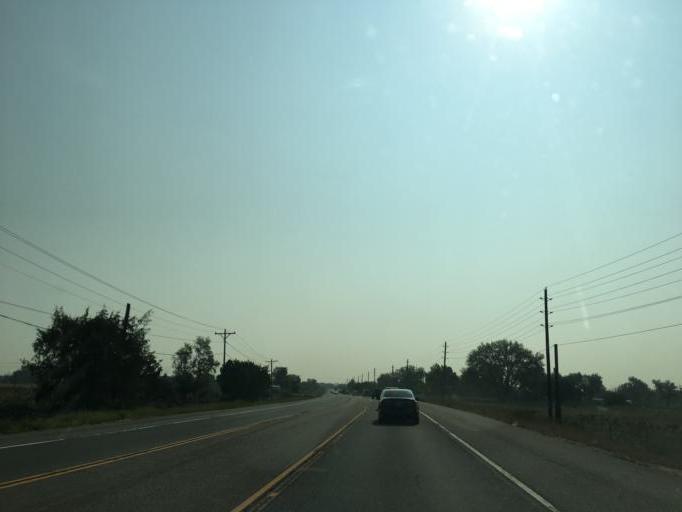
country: US
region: Colorado
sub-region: Adams County
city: Brighton
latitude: 39.9870
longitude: -104.8404
